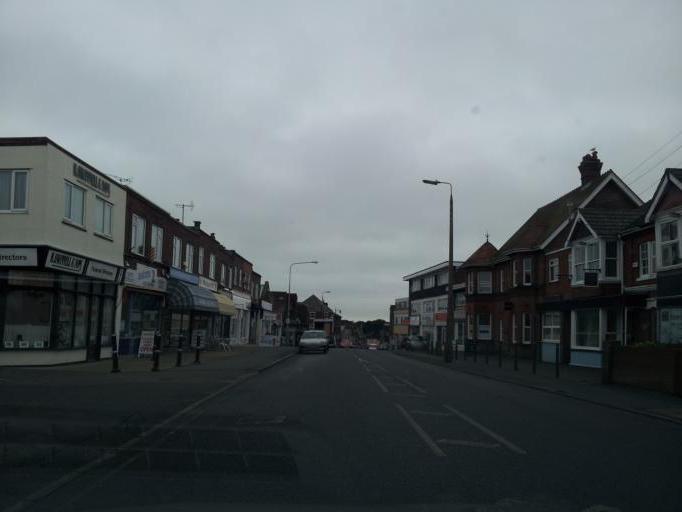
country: GB
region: England
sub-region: Essex
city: Dovercourt
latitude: 51.9365
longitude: 1.2771
